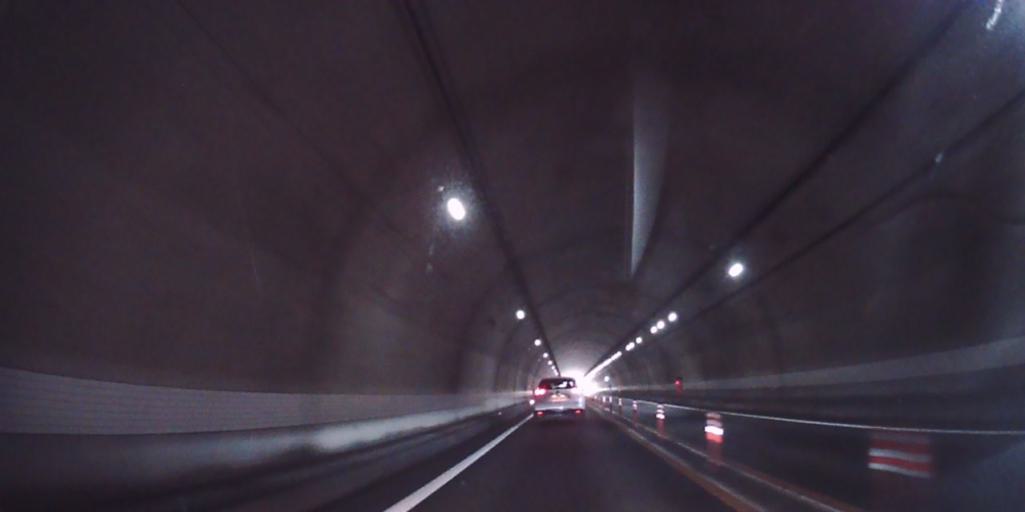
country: JP
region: Hokkaido
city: Niseko Town
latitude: 42.5945
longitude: 140.6728
